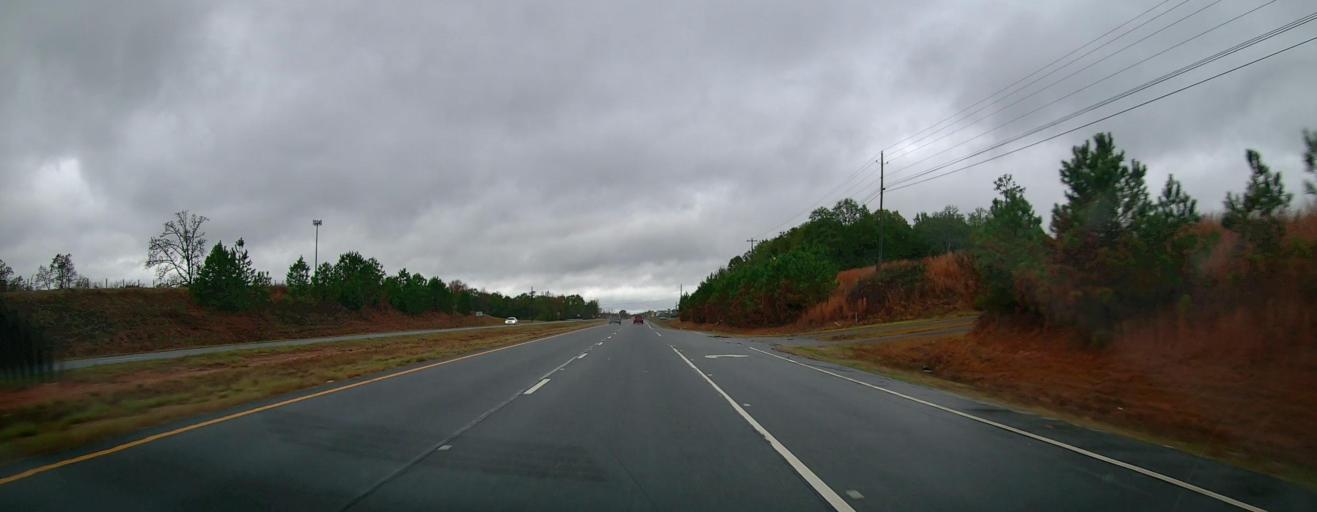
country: US
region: Georgia
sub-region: Jackson County
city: Nicholson
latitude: 34.1499
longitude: -83.4394
